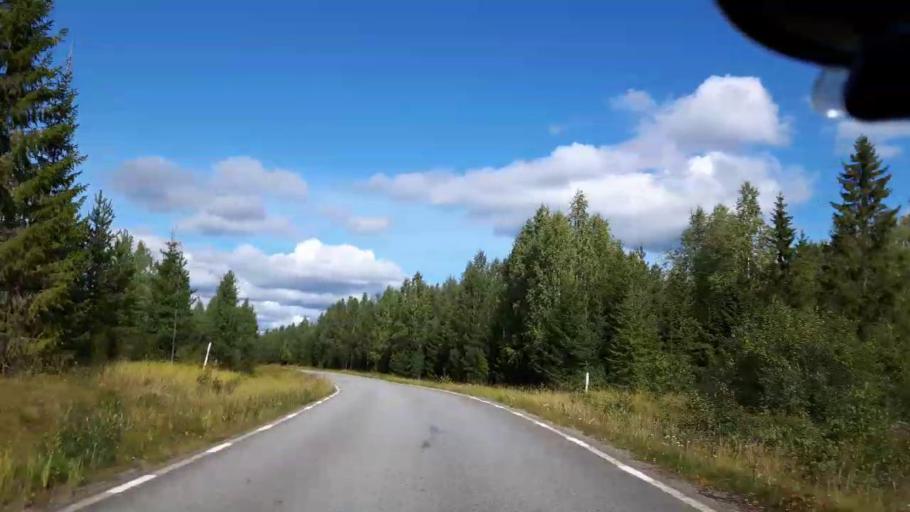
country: SE
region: Jaemtland
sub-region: OEstersunds Kommun
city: Brunflo
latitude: 63.2105
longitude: 15.2488
